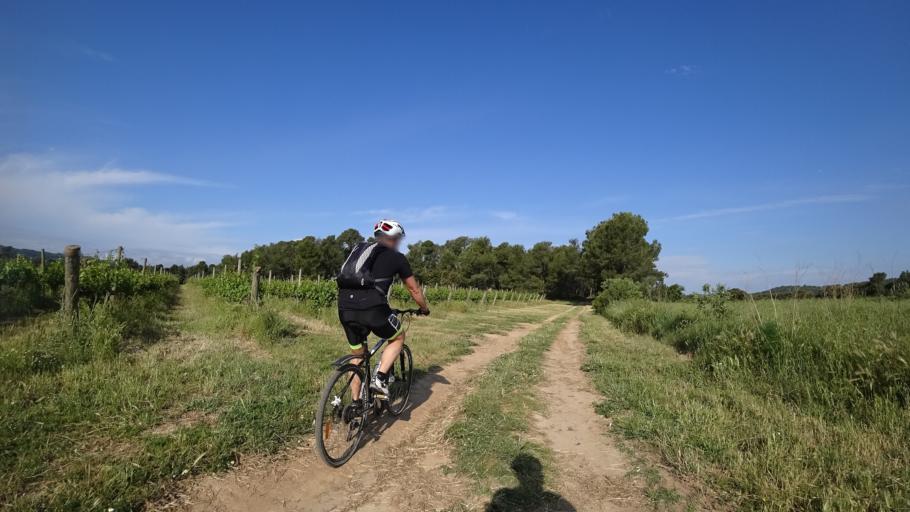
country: FR
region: Languedoc-Roussillon
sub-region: Departement de l'Aude
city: Lezignan-Corbieres
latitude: 43.2372
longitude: 2.7420
